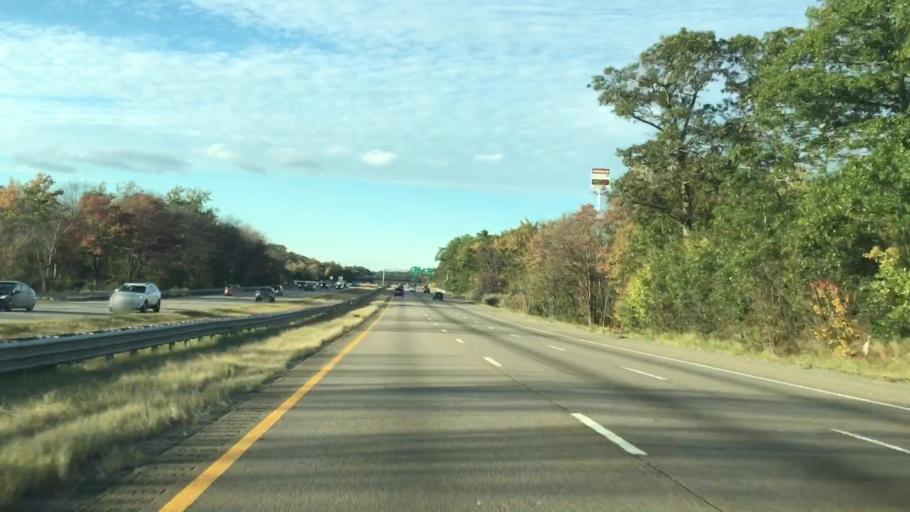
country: US
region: Massachusetts
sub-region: Norfolk County
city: Randolph
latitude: 42.1506
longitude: -71.0675
